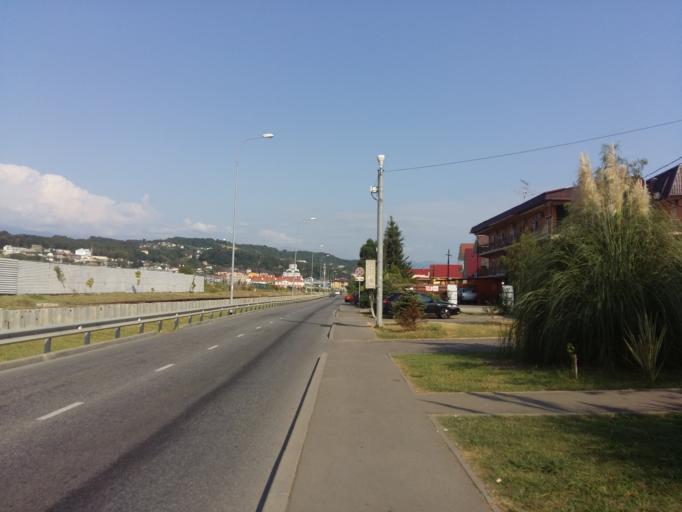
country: RU
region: Krasnodarskiy
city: Adler
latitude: 43.4151
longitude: 39.9595
